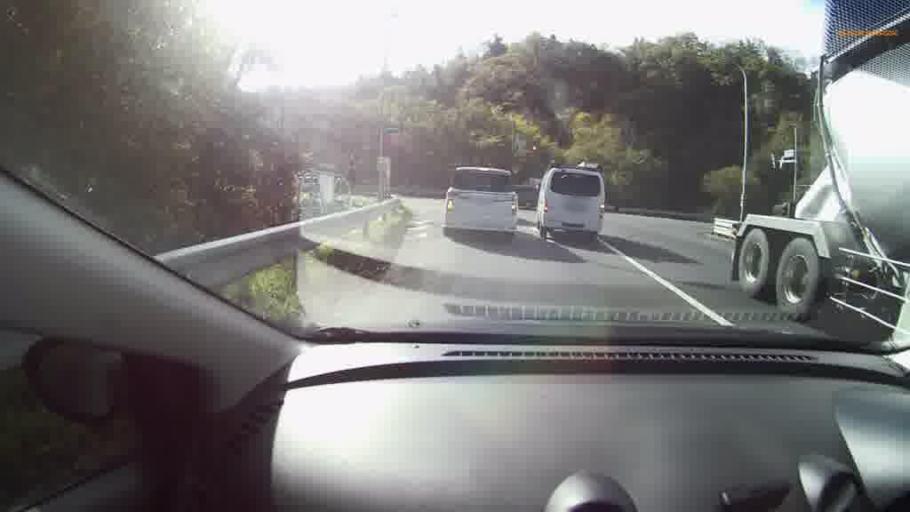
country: JP
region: Hokkaido
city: Kushiro
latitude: 43.0007
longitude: 144.5015
